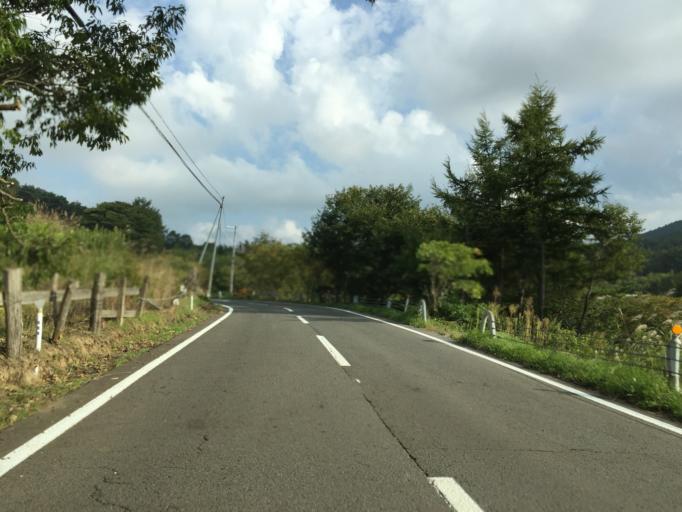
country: JP
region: Fukushima
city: Funehikimachi-funehiki
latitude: 37.5856
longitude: 140.7157
